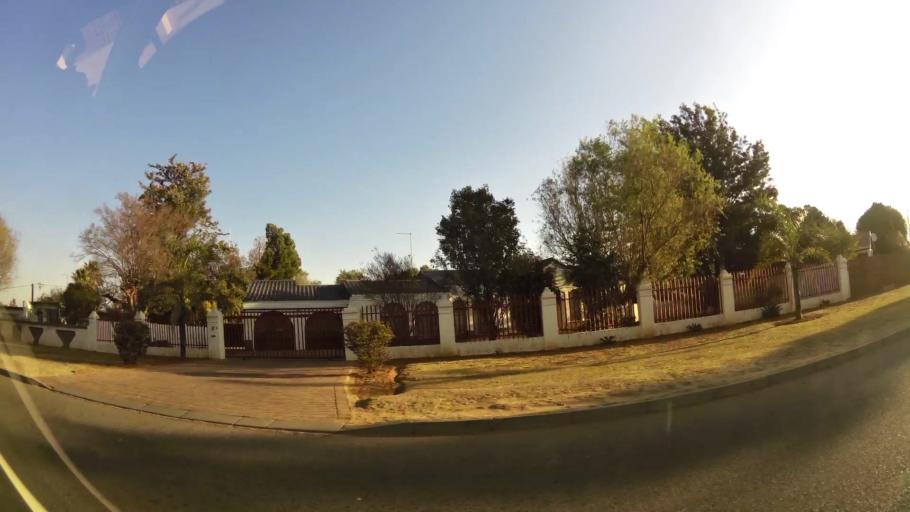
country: ZA
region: Gauteng
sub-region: West Rand District Municipality
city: Randfontein
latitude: -26.2104
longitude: 27.6574
